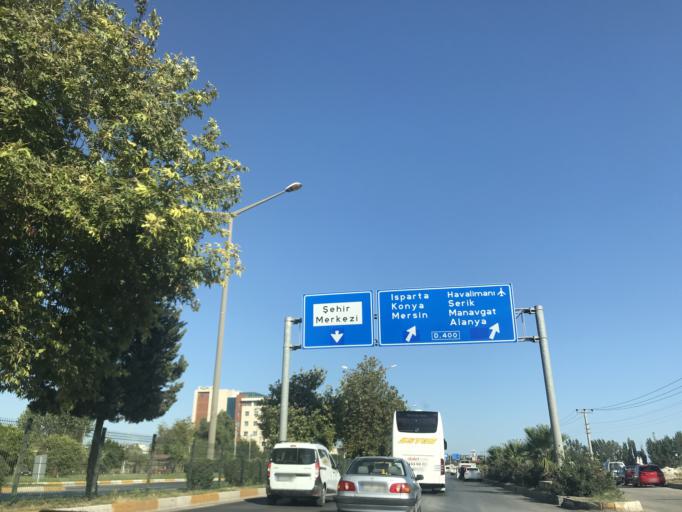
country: TR
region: Antalya
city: Antalya
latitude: 36.9031
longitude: 30.7566
